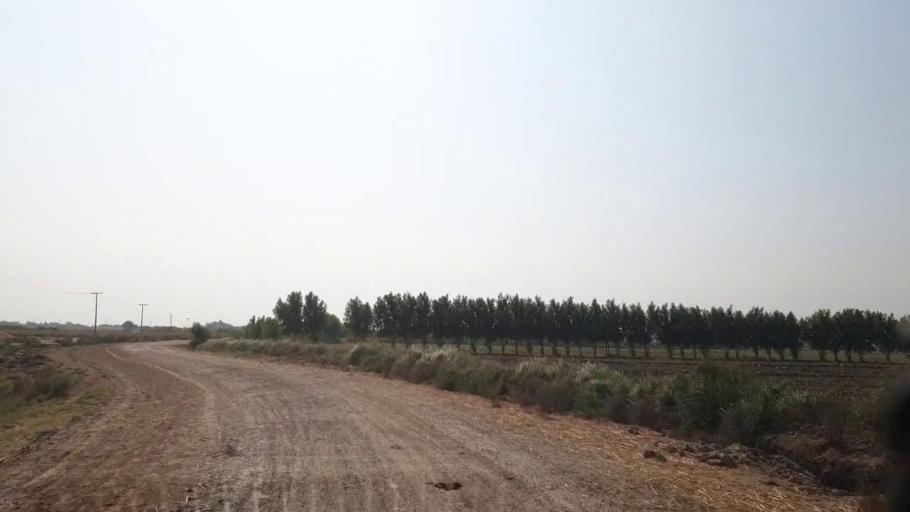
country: PK
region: Sindh
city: Tando Muhammad Khan
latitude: 25.0484
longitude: 68.4517
